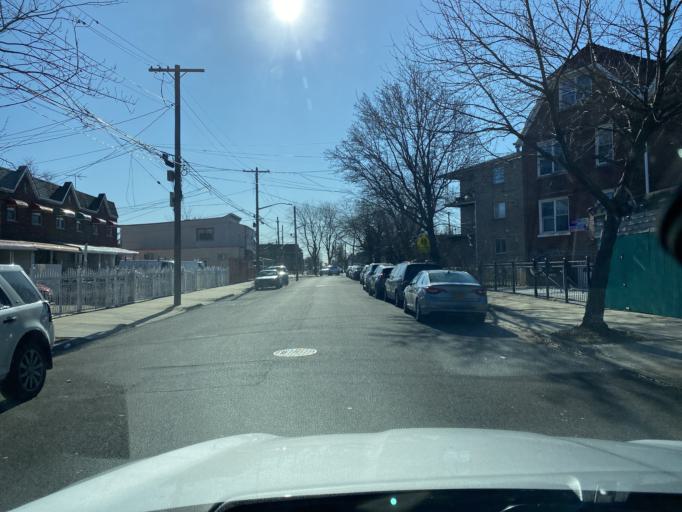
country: US
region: New York
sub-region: Bronx
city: The Bronx
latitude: 40.8162
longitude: -73.8599
